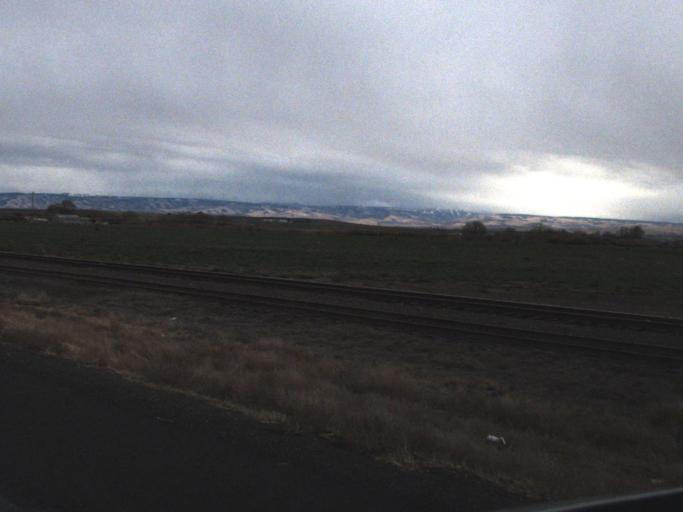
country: US
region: Washington
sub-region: Walla Walla County
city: Garrett
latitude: 46.0396
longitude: -118.6571
